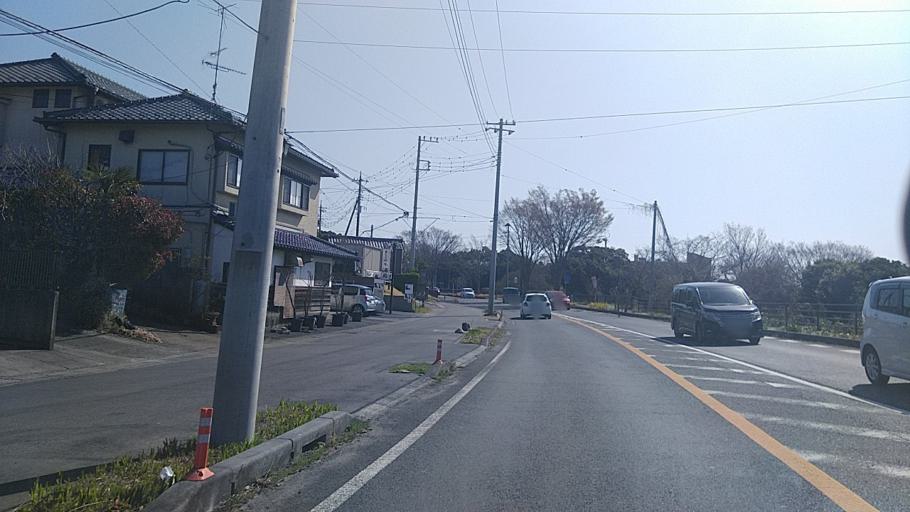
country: JP
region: Ibaraki
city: Toride
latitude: 35.8901
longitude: 140.0928
